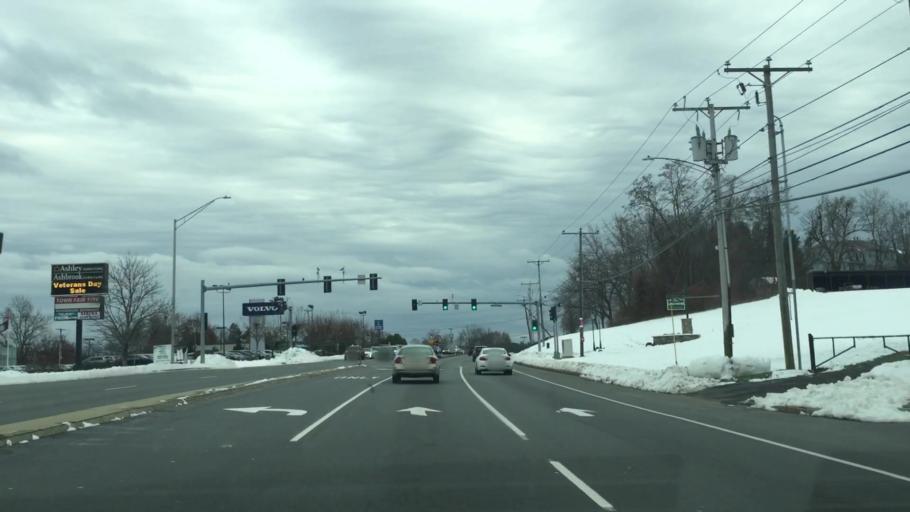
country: US
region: New Hampshire
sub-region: Hillsborough County
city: Hudson
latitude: 42.7203
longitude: -71.4428
